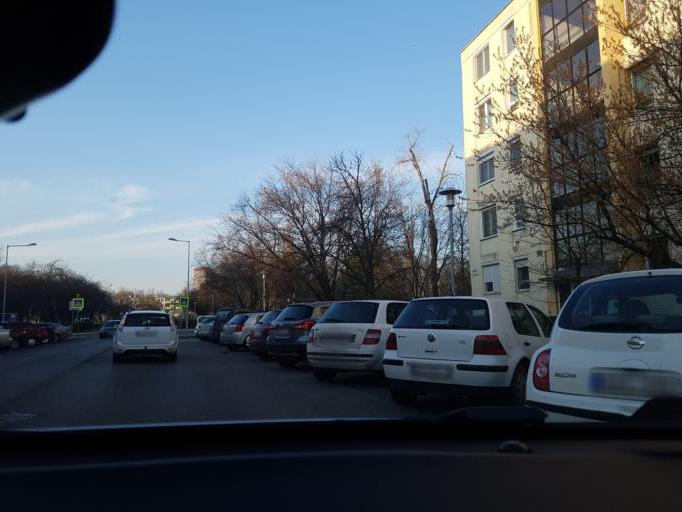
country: HU
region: Budapest
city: Budapest XX. keruelet
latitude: 47.4637
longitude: 19.1153
